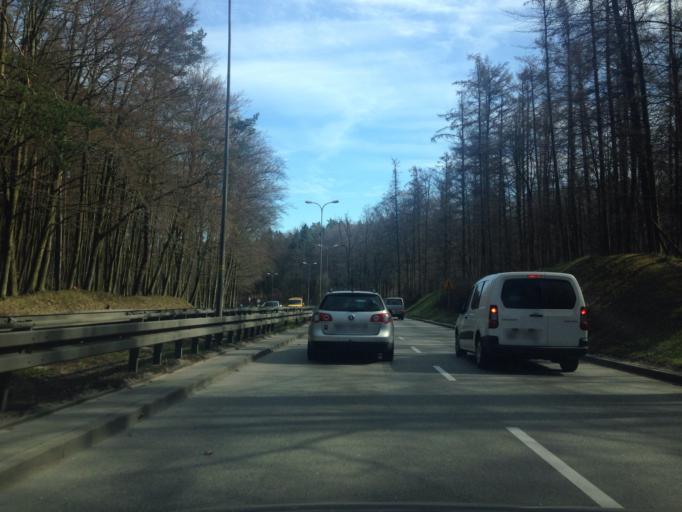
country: PL
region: Pomeranian Voivodeship
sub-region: Powiat gdanski
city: Kowale
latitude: 54.3737
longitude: 18.5403
